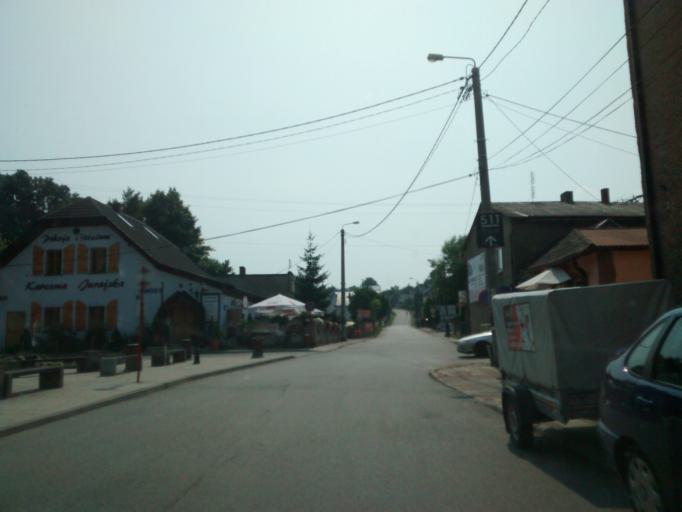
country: PL
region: Silesian Voivodeship
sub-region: Powiat zawiercianski
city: Ogrodzieniec
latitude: 50.4541
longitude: 19.5478
